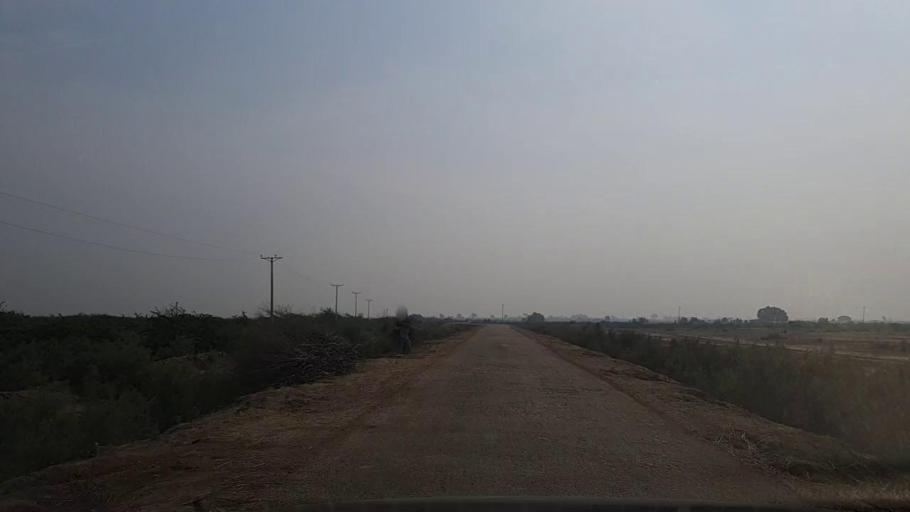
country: PK
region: Sindh
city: Mirpur Sakro
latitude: 24.3870
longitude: 67.7526
